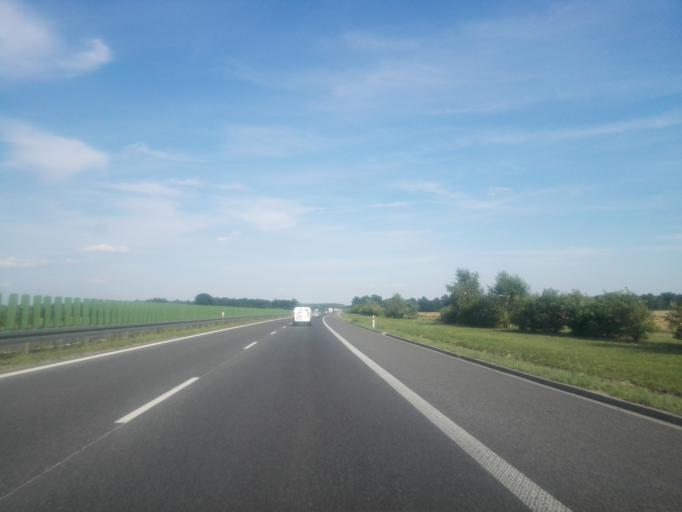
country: PL
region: Lower Silesian Voivodeship
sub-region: Powiat olesnicki
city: Olesnica
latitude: 51.2338
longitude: 17.4081
